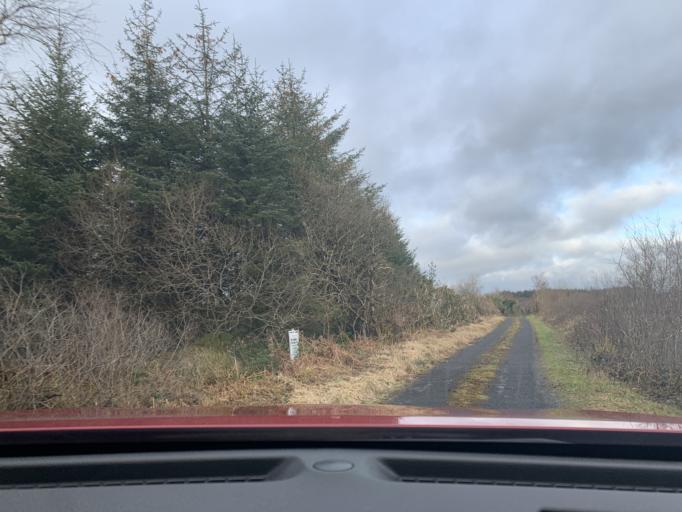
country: IE
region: Connaught
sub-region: Roscommon
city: Ballaghaderreen
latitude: 53.9282
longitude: -8.5603
